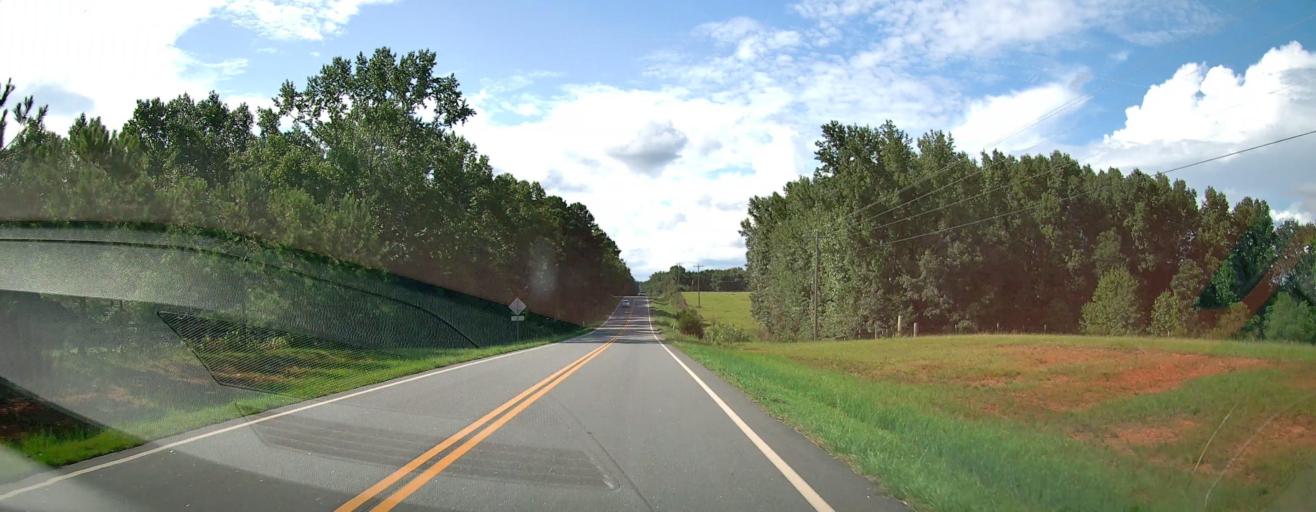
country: US
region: Georgia
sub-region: Upson County
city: Hannahs Mill
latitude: 32.9509
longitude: -84.4589
